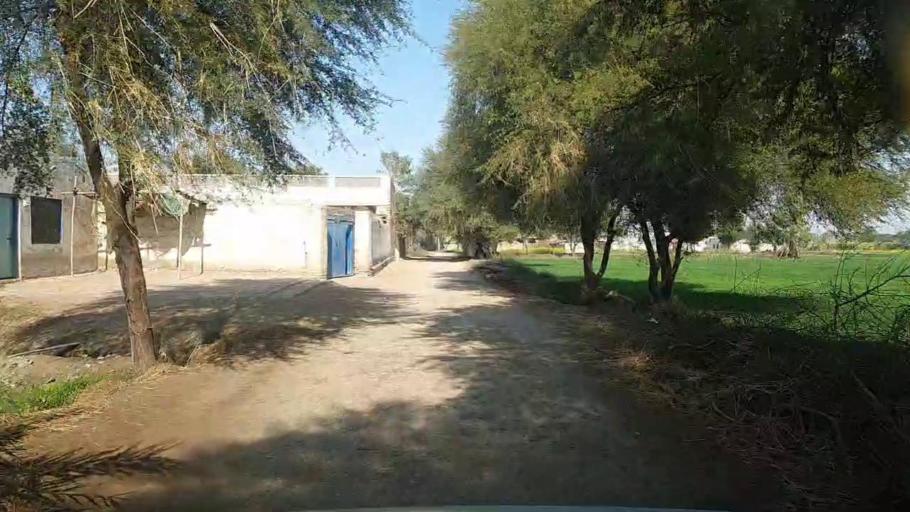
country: PK
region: Sindh
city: Khairpur
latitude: 28.0584
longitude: 69.6729
